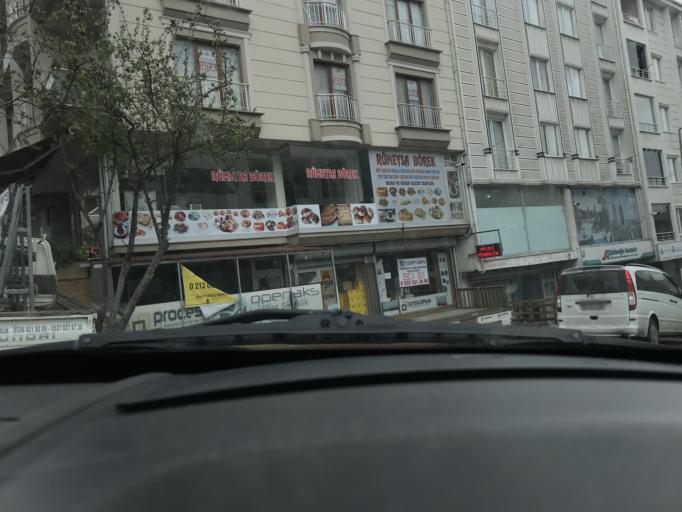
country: TR
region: Istanbul
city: Yakuplu
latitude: 41.0059
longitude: 28.6881
